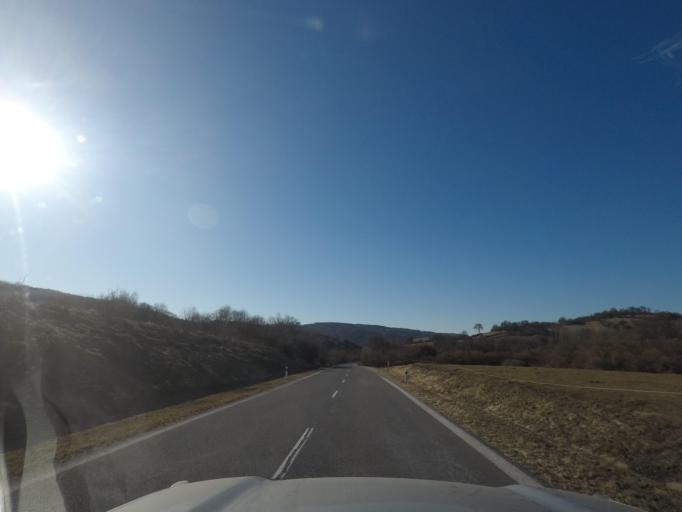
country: PL
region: Subcarpathian Voivodeship
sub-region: Powiat sanocki
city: Komancza
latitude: 49.1600
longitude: 22.0493
